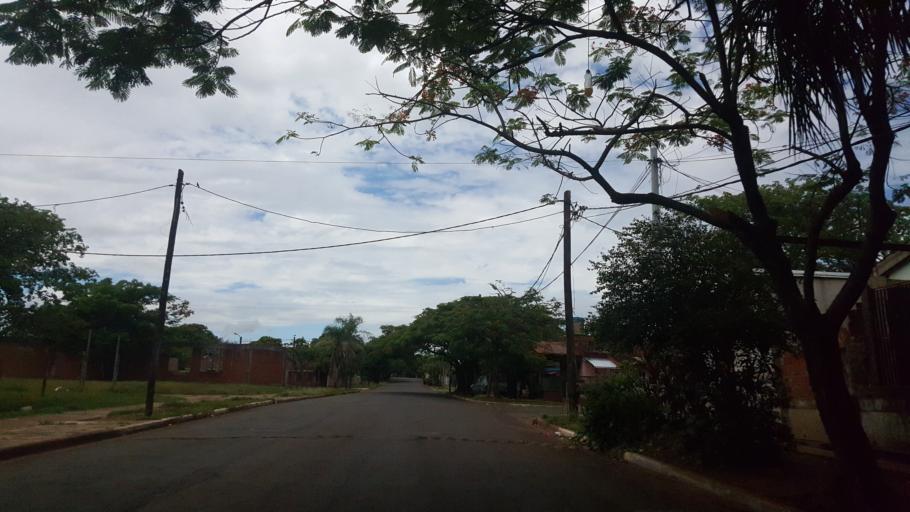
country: AR
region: Misiones
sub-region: Departamento de Capital
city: Posadas
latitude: -27.4216
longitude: -55.8863
